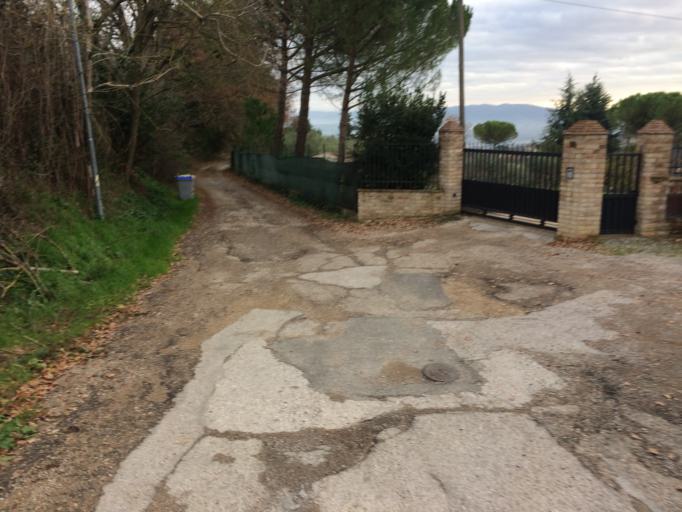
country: IT
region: Umbria
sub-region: Provincia di Perugia
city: Perugia
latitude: 43.1018
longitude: 12.4035
